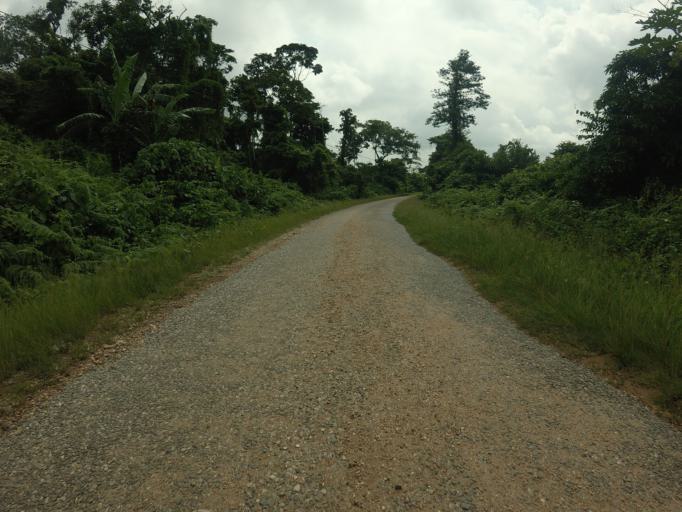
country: GH
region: Volta
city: Kpandu
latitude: 6.8437
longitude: 0.4340
